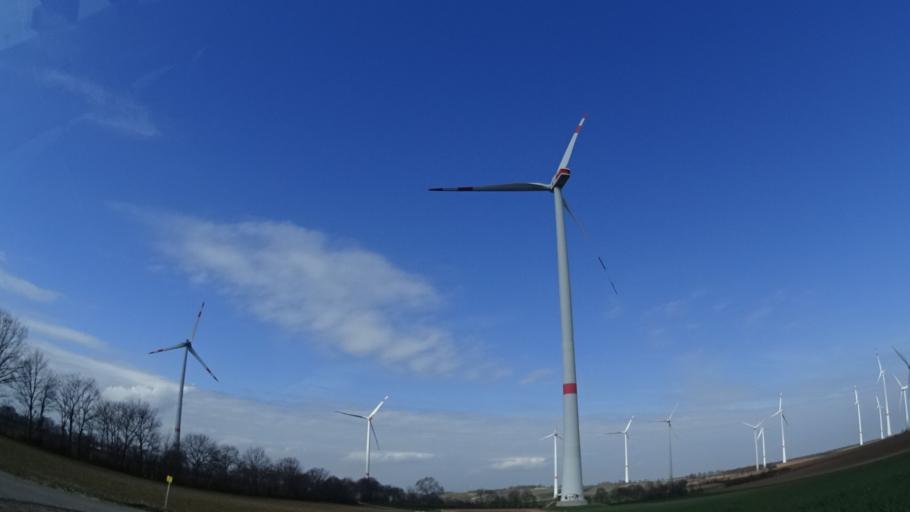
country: DE
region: Rheinland-Pfalz
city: Bornheim
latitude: 49.7538
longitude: 8.0610
